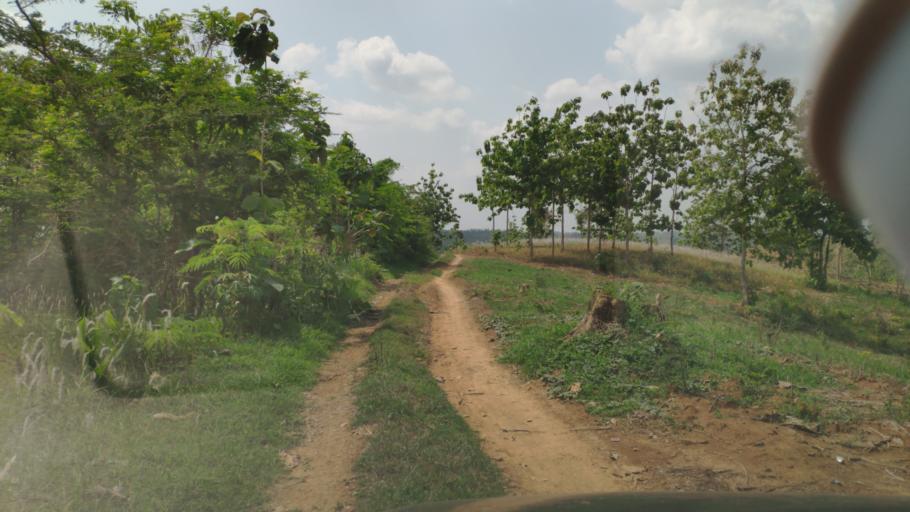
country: ID
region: Central Java
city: Gaplokan
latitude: -6.9136
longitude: 111.2635
